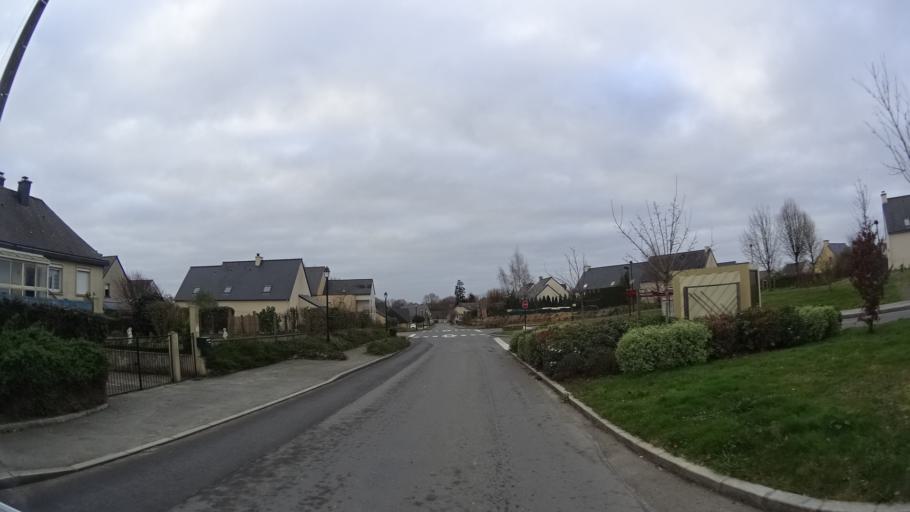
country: FR
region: Brittany
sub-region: Departement d'Ille-et-Vilaine
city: Saint-Gilles
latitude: 48.1940
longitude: -1.8321
